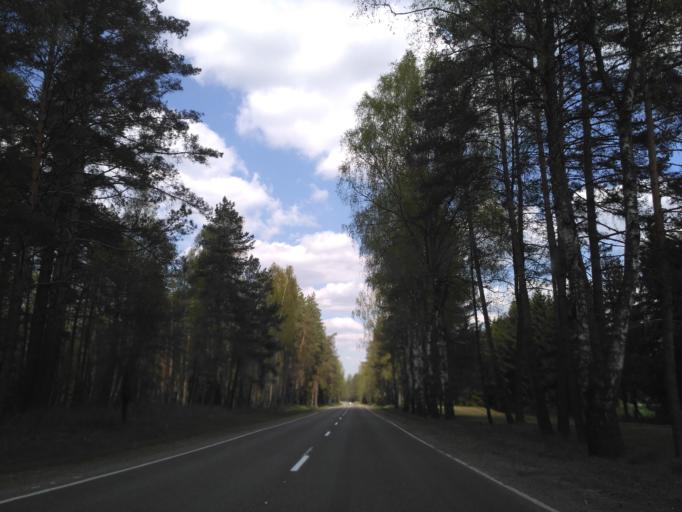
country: BY
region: Minsk
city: Myadzyel
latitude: 54.7356
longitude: 26.9435
